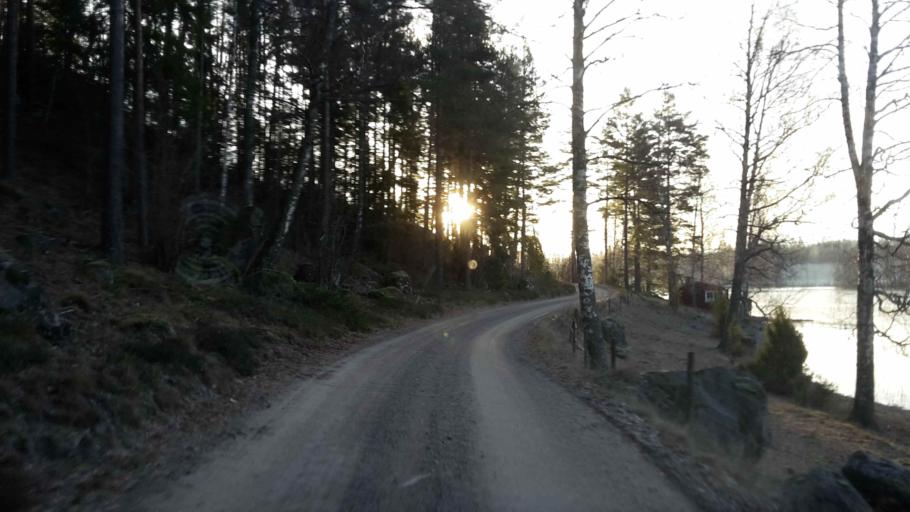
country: SE
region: OEstergoetland
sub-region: Atvidabergs Kommun
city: Atvidaberg
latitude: 58.2716
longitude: 16.1208
